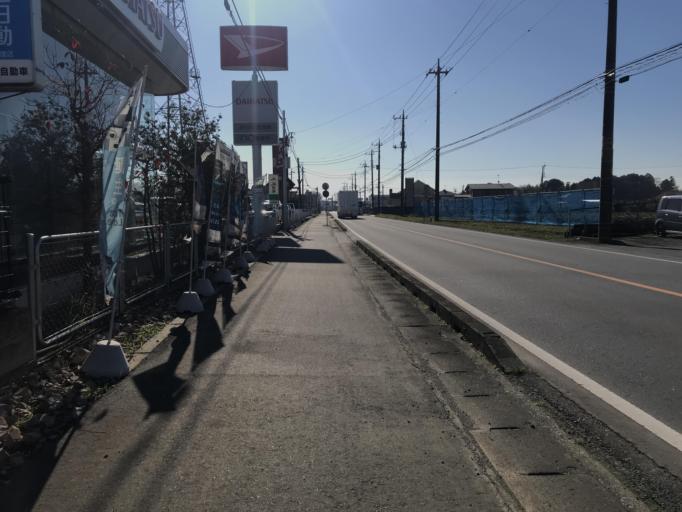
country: JP
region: Ibaraki
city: Sakai
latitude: 36.1647
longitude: 139.8095
